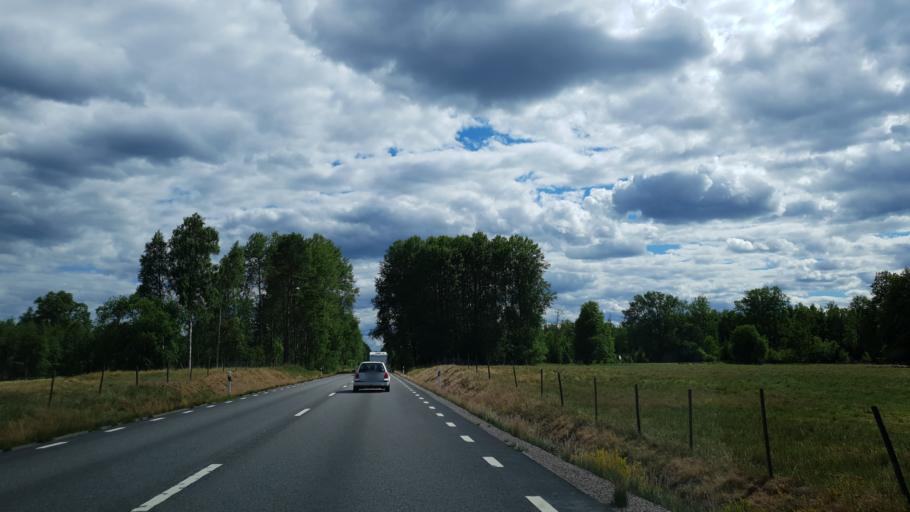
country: SE
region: Kronoberg
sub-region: Lessebo Kommun
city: Lessebo
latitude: 56.7943
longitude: 15.4127
